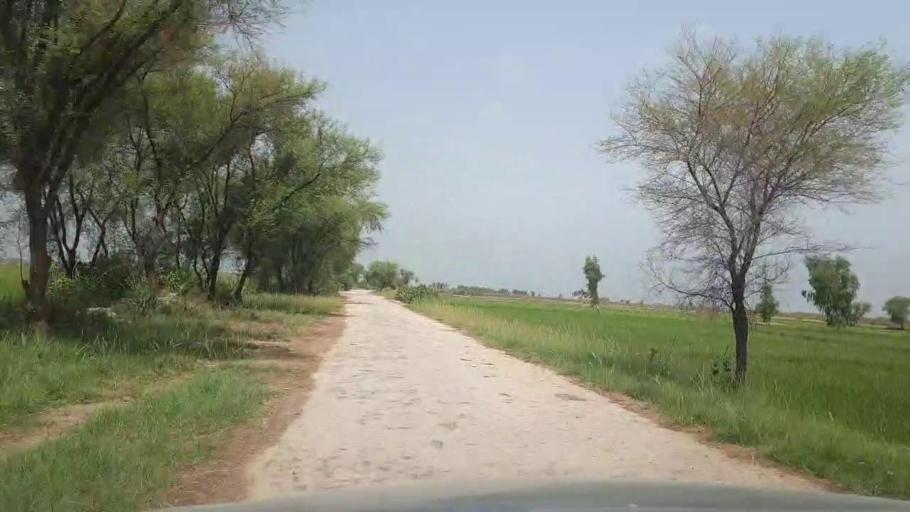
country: PK
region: Sindh
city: Garhi Yasin
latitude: 27.9489
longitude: 68.3674
